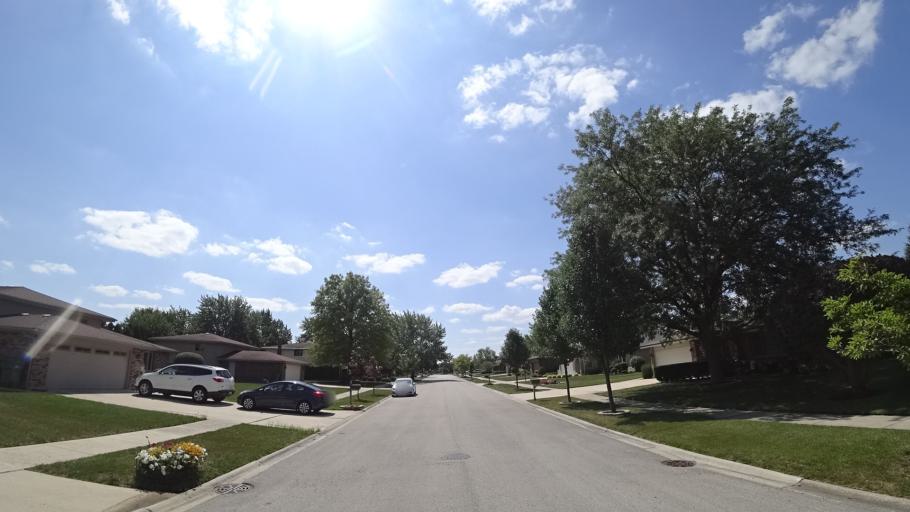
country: US
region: Illinois
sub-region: Cook County
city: Orland Park
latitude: 41.6372
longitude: -87.8480
